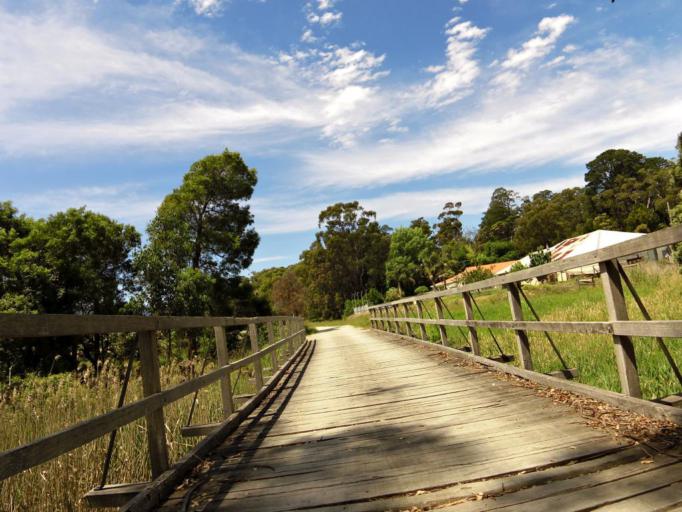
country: AU
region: Victoria
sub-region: Yarra Ranges
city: Launching Place
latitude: -37.7751
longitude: 145.5780
